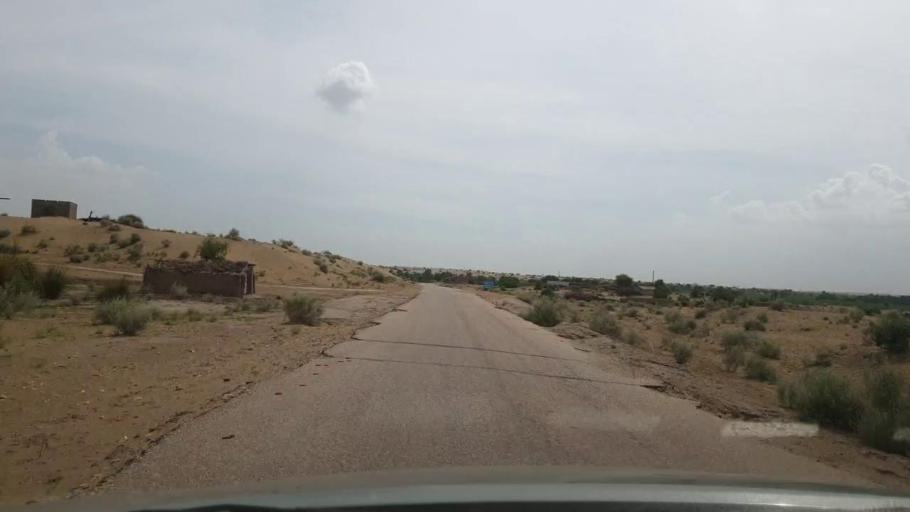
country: PK
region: Sindh
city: Kot Diji
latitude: 27.1678
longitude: 69.0379
